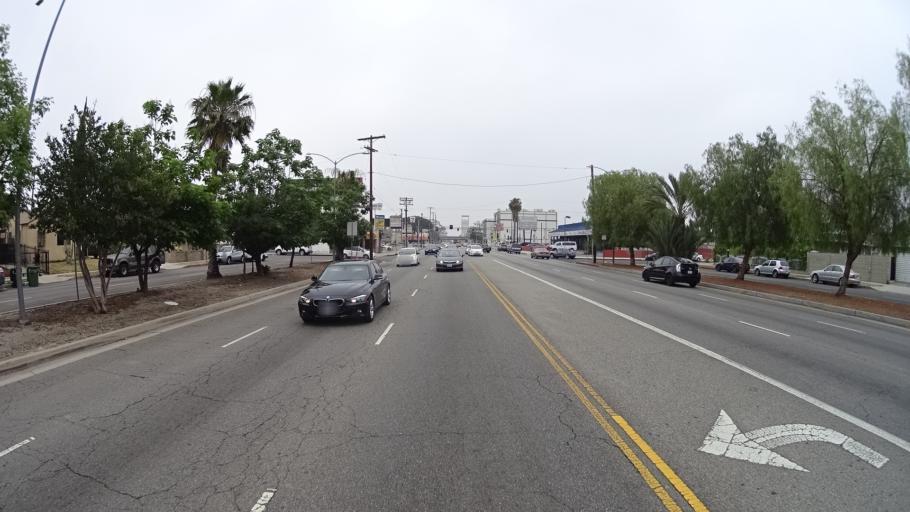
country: US
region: California
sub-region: Los Angeles County
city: North Hollywood
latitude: 34.1867
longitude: -118.4069
